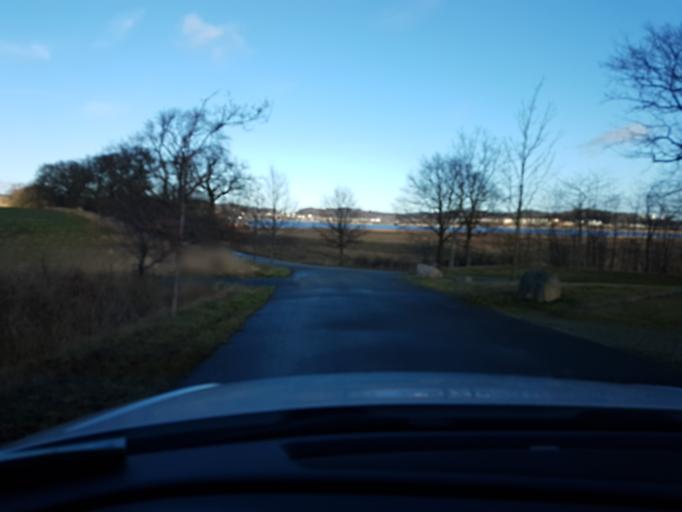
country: DE
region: Mecklenburg-Vorpommern
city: Ostseebad Sellin
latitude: 54.3551
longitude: 13.6823
